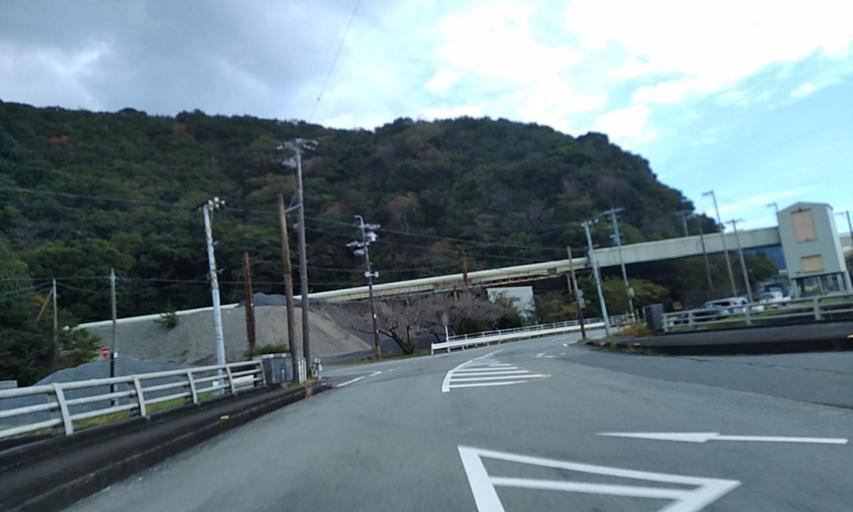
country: JP
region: Mie
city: Ise
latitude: 34.2794
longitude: 136.5007
